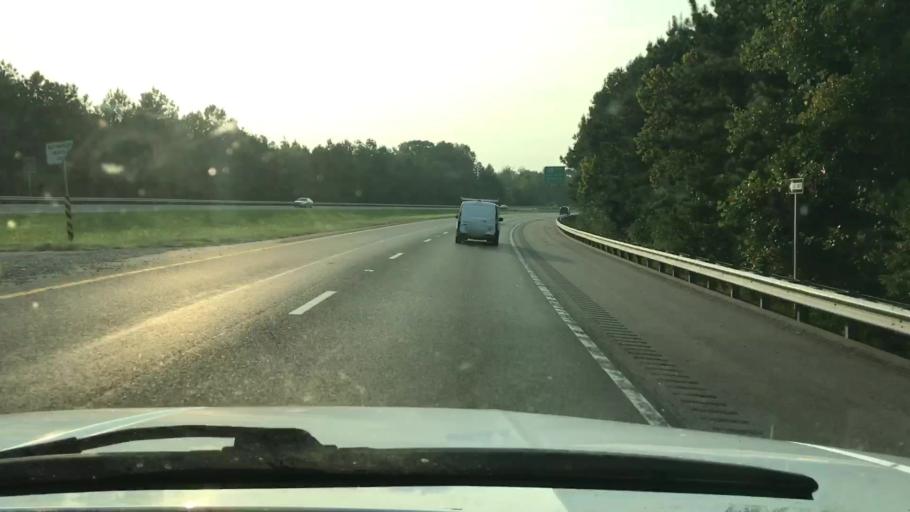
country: US
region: Virginia
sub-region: Chesterfield County
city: Brandermill
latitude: 37.4103
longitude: -77.6137
